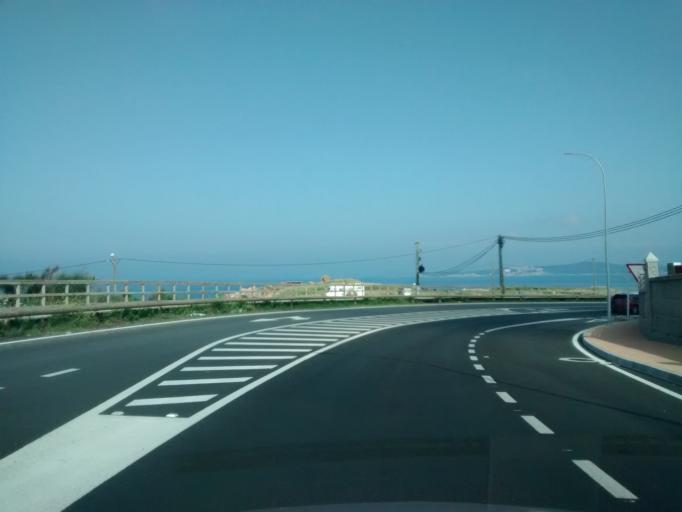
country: ES
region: Galicia
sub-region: Provincia de Pontevedra
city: O Grove
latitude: 42.4284
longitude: -8.8729
